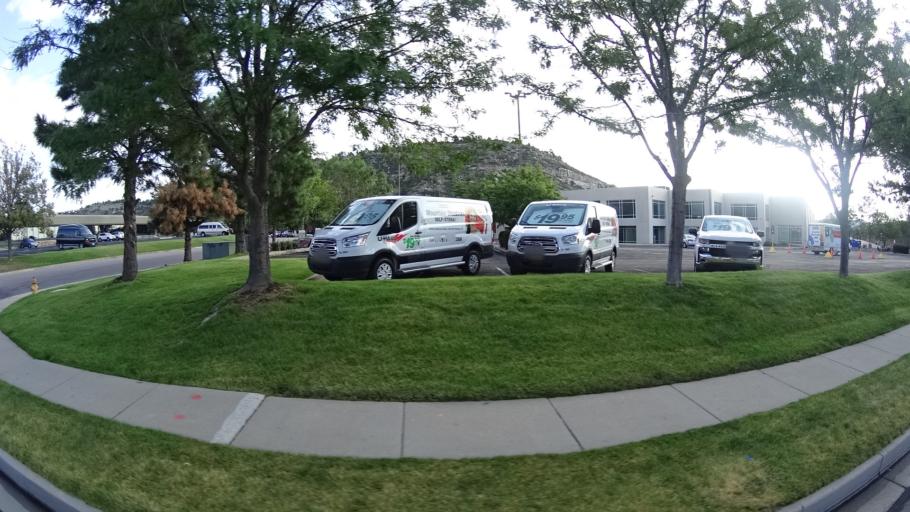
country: US
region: Colorado
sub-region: El Paso County
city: Colorado Springs
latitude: 38.9002
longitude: -104.8521
